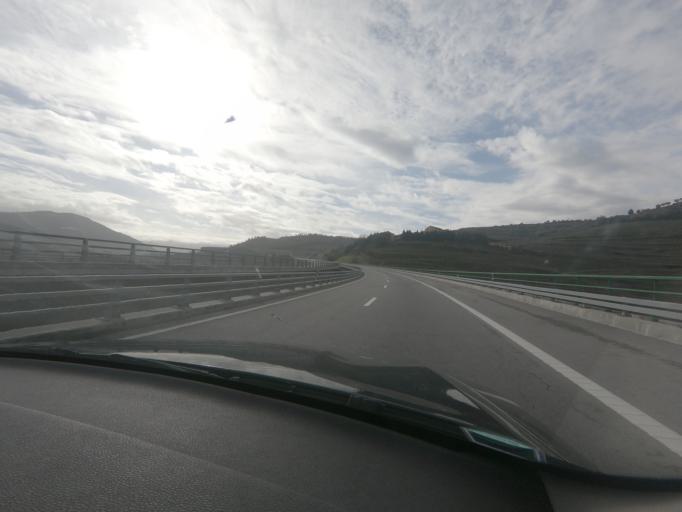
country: PT
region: Vila Real
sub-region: Peso da Regua
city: Peso da Regua
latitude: 41.1745
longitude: -7.7675
